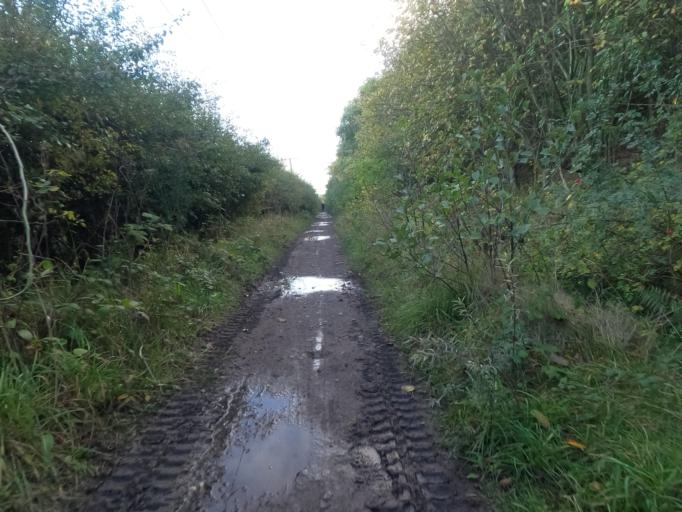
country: GB
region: England
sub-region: Northumberland
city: Seghill
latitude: 55.0728
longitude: -1.5487
